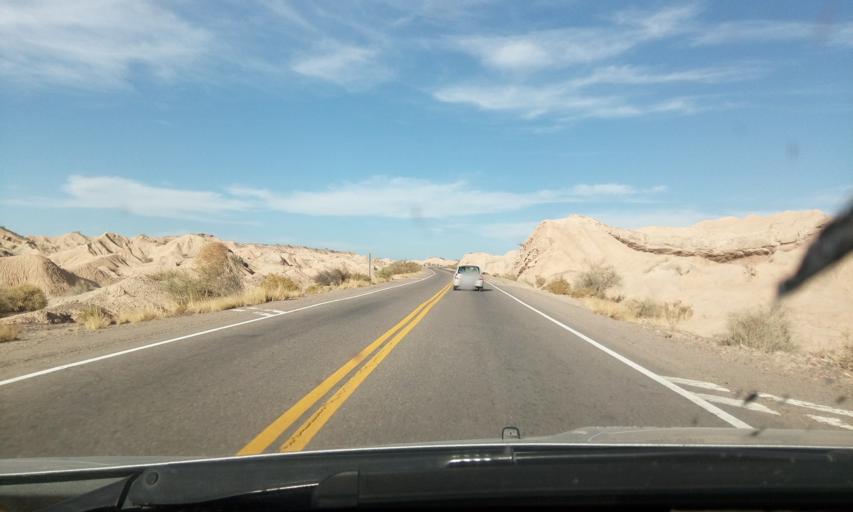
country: AR
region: San Juan
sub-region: Departamento de Rivadavia
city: Rivadavia
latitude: -31.4482
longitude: -68.6421
